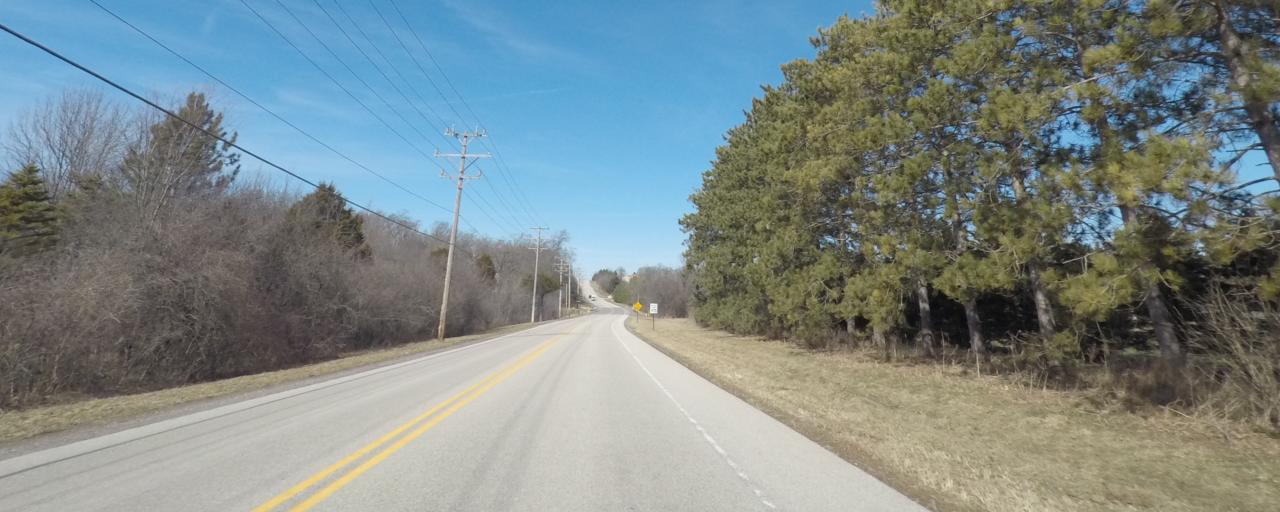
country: US
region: Wisconsin
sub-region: Waukesha County
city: Merton
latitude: 43.1465
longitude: -88.3268
